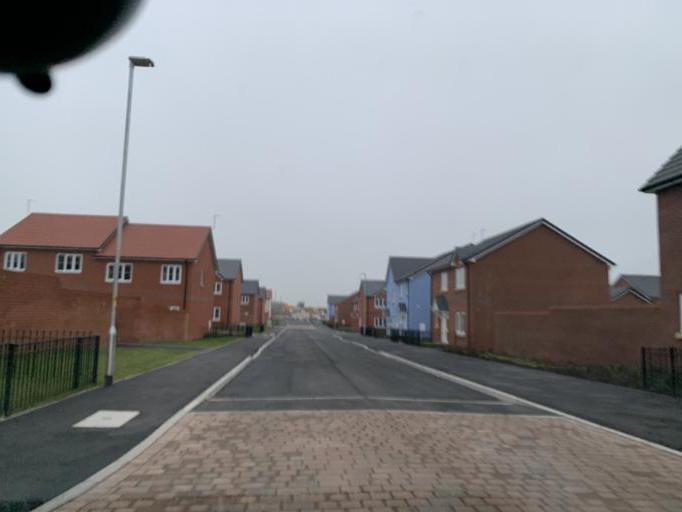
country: GB
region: England
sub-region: Wiltshire
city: Durrington
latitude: 51.1999
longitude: -1.7952
